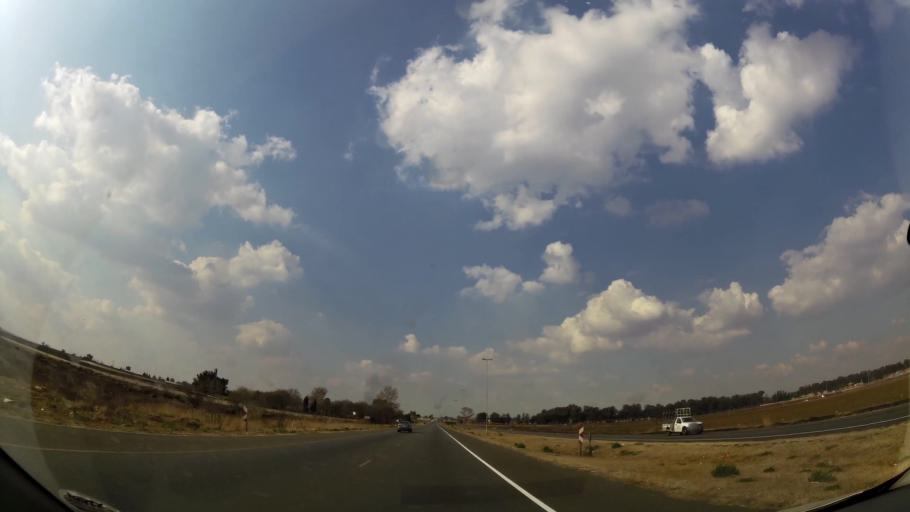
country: ZA
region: Gauteng
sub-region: Ekurhuleni Metropolitan Municipality
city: Germiston
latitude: -26.2930
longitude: 28.2178
